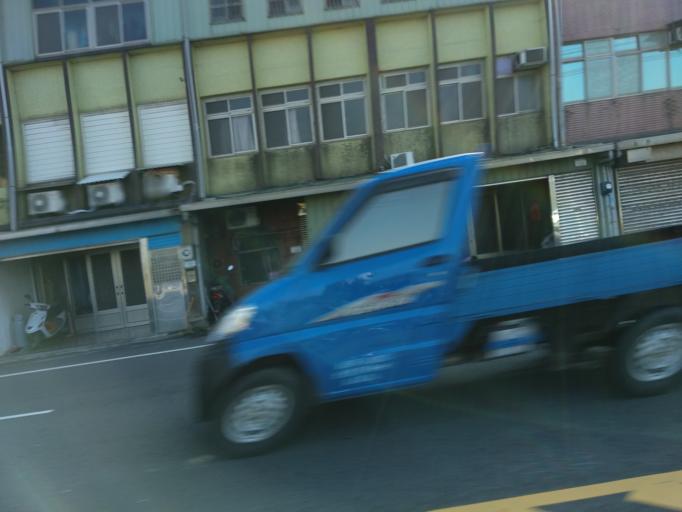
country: TW
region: Taiwan
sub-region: Hsinchu
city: Zhubei
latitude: 24.9854
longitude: 121.0520
